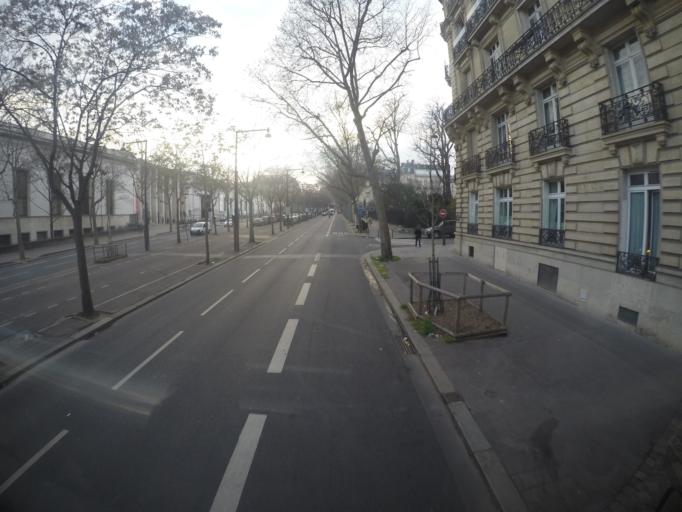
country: FR
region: Ile-de-France
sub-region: Departement des Hauts-de-Seine
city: Levallois-Perret
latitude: 48.8651
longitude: 2.2981
